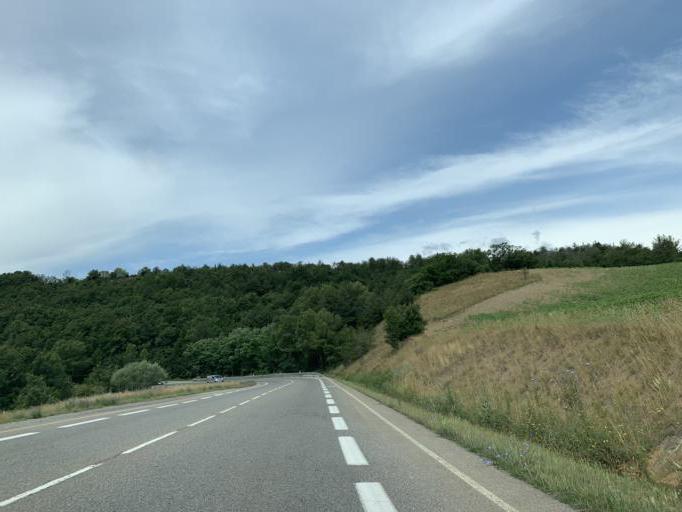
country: FR
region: Provence-Alpes-Cote d'Azur
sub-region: Departement des Hautes-Alpes
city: Gap
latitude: 44.5495
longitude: 6.0261
